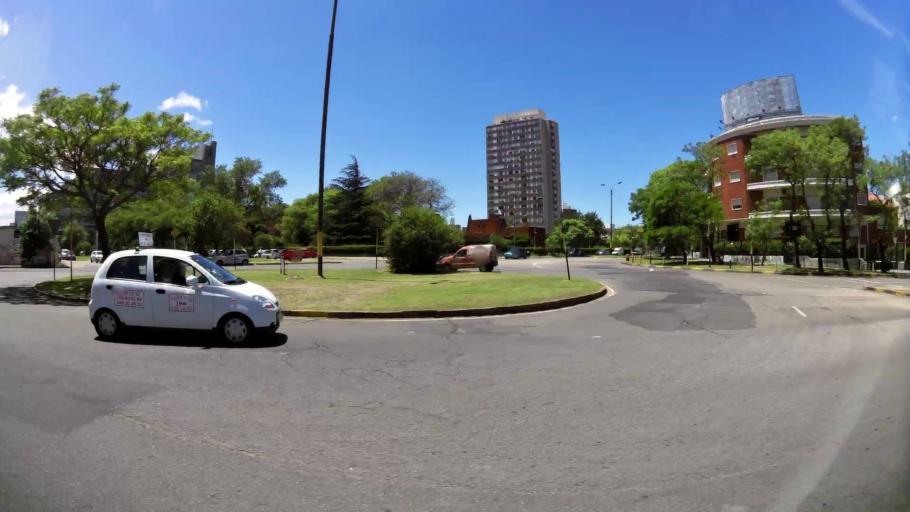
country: UY
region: Montevideo
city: Montevideo
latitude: -34.8940
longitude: -56.1513
